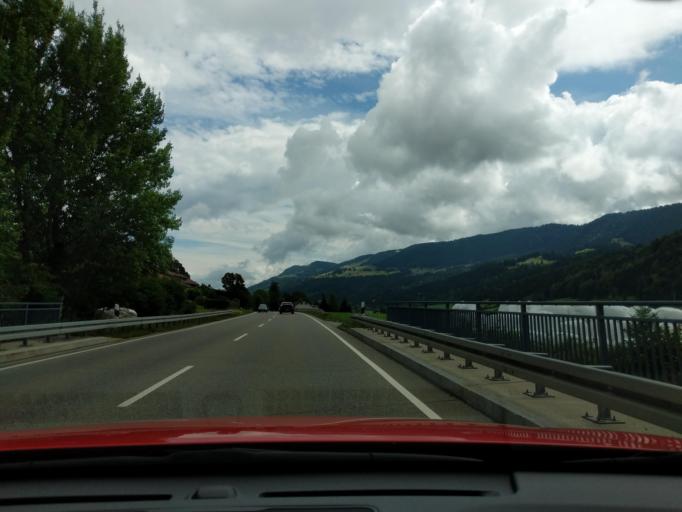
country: DE
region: Bavaria
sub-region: Swabia
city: Oberstaufen
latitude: 47.5547
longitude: 10.0590
